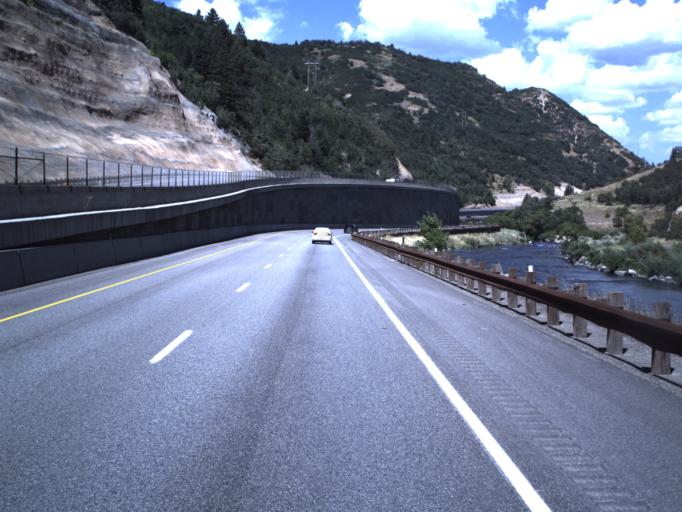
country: US
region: Utah
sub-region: Utah County
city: Orem
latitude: 40.3702
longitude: -111.5553
